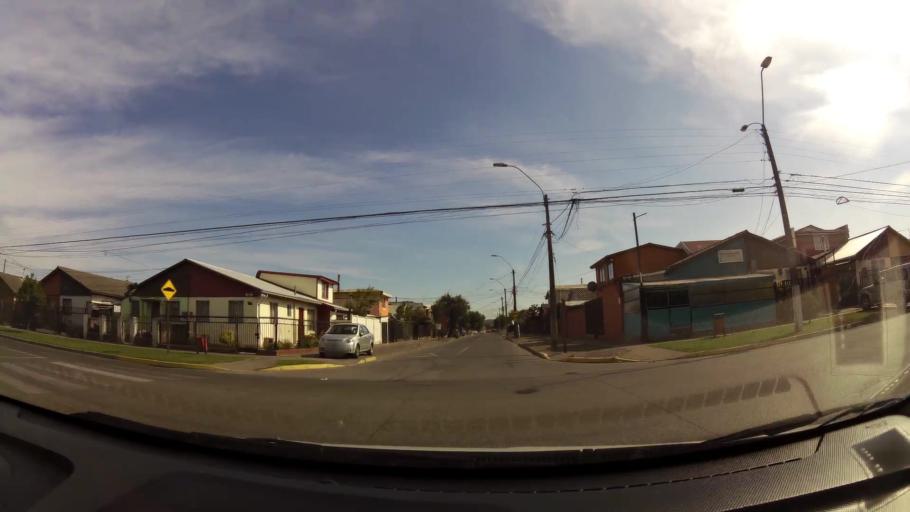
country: CL
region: Biobio
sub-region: Provincia de Concepcion
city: Talcahuano
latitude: -36.7868
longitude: -73.1064
